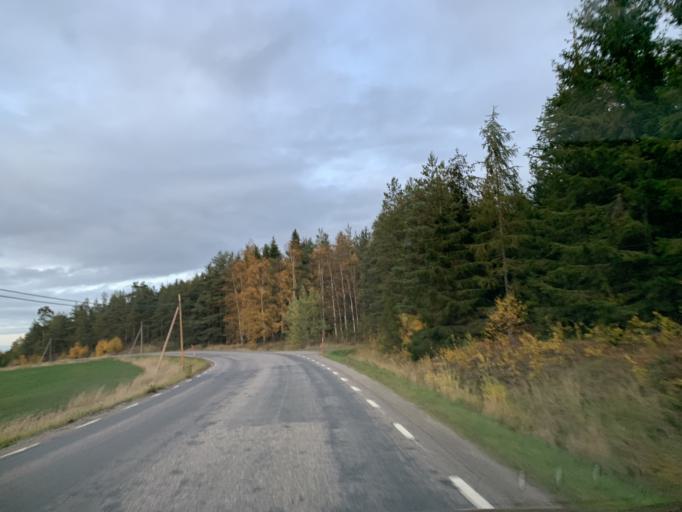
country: SE
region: Stockholm
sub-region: Nynashamns Kommun
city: Osmo
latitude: 58.9427
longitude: 17.7613
